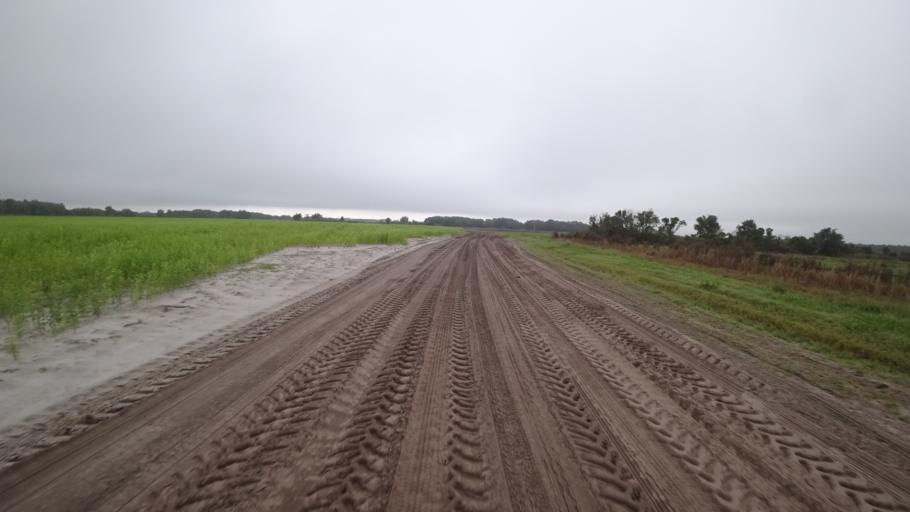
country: US
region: Florida
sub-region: Sarasota County
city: Warm Mineral Springs
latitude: 27.2871
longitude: -82.1677
